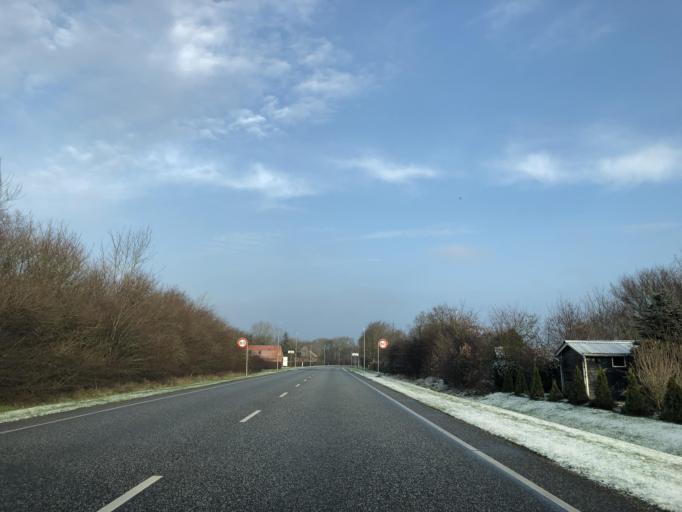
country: DK
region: Central Jutland
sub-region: Ringkobing-Skjern Kommune
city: Tarm
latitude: 55.8966
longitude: 8.5140
